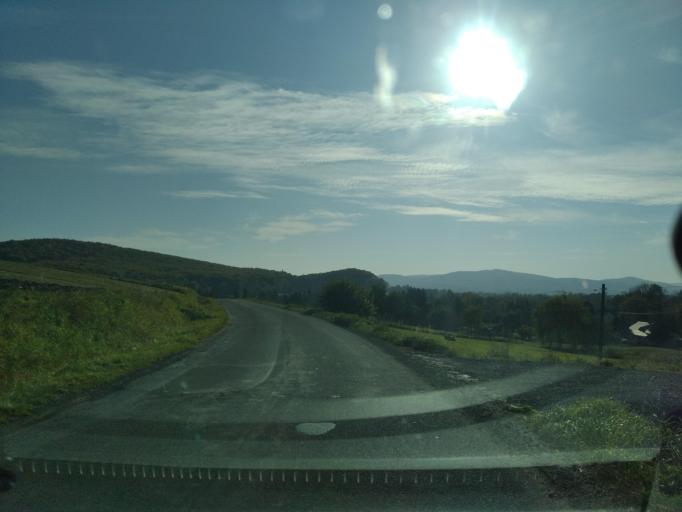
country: PL
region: Subcarpathian Voivodeship
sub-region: Powiat sanocki
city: Besko
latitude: 49.5774
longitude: 21.9476
